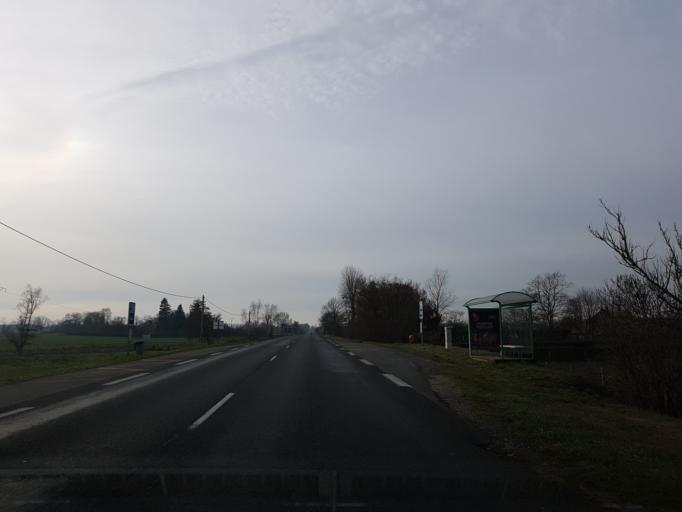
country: FR
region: Auvergne
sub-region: Departement de l'Allier
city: Lusigny
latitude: 46.5885
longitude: 3.4685
